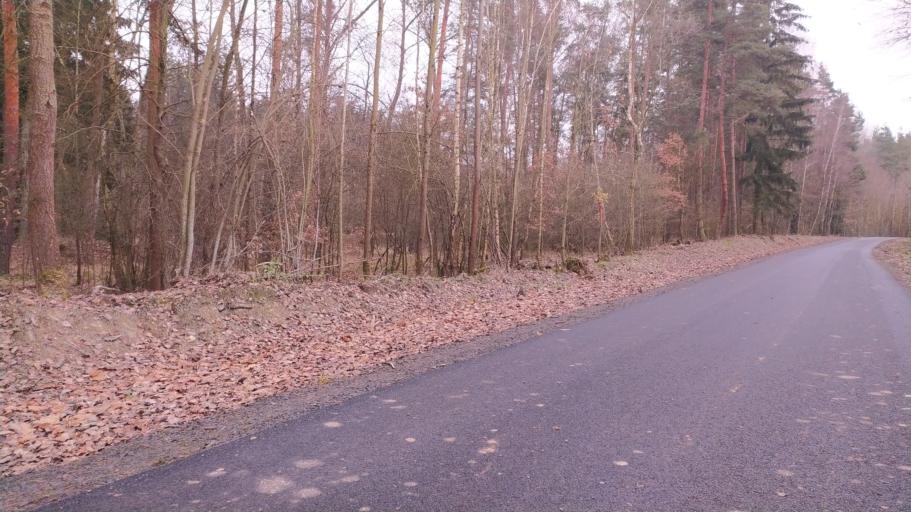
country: DE
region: Bavaria
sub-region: Upper Franconia
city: Schirnding
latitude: 50.1002
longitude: 12.2735
